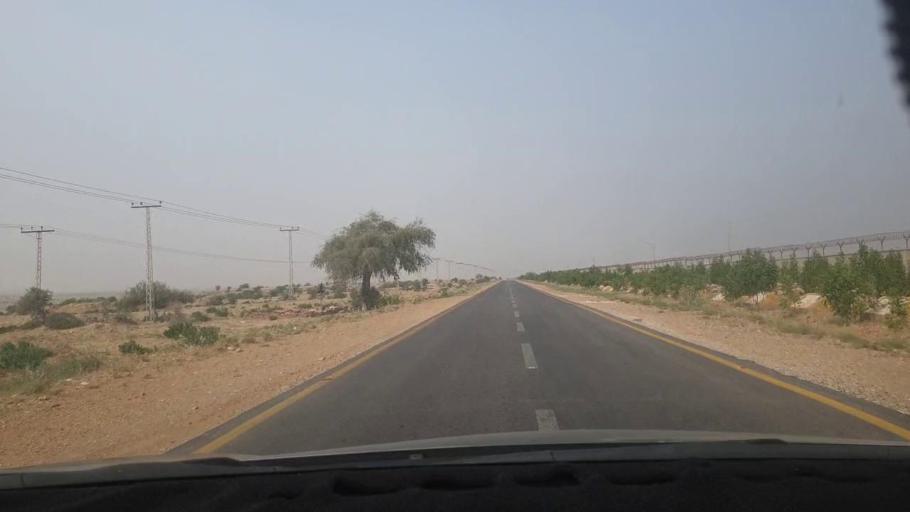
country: PK
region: Sindh
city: Jamshoro
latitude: 25.5449
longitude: 68.3203
